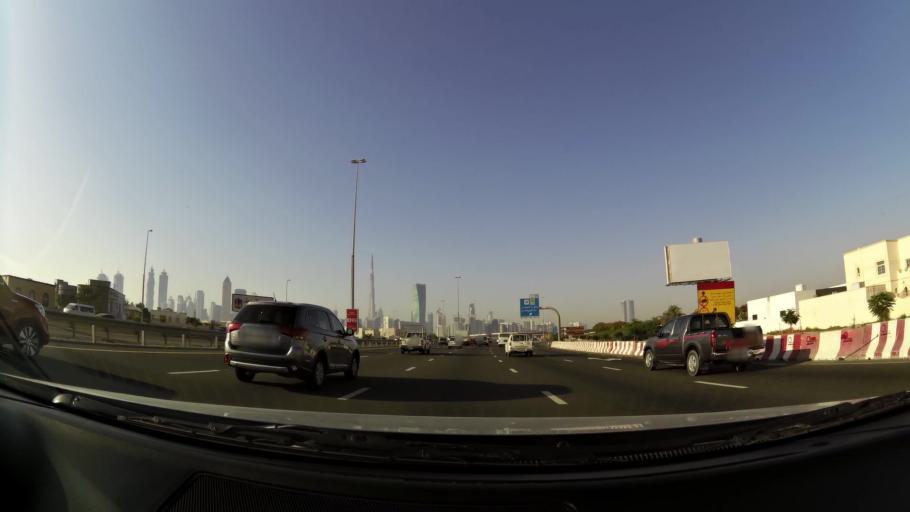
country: AE
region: Dubai
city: Dubai
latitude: 25.1634
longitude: 55.2633
